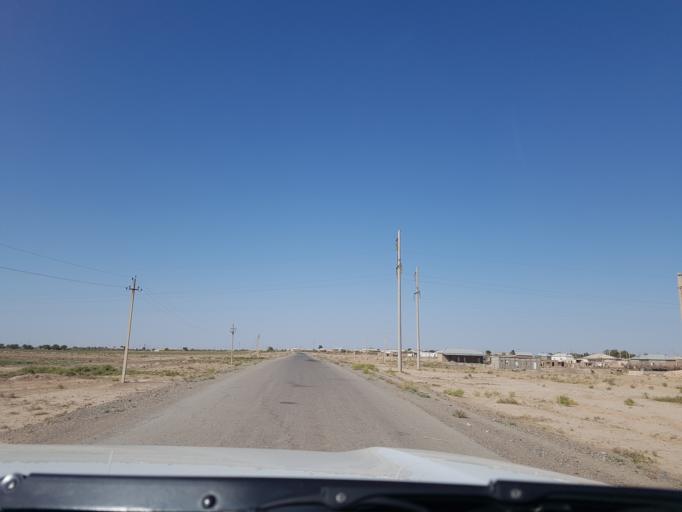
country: IR
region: Razavi Khorasan
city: Sarakhs
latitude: 36.5084
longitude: 61.2533
